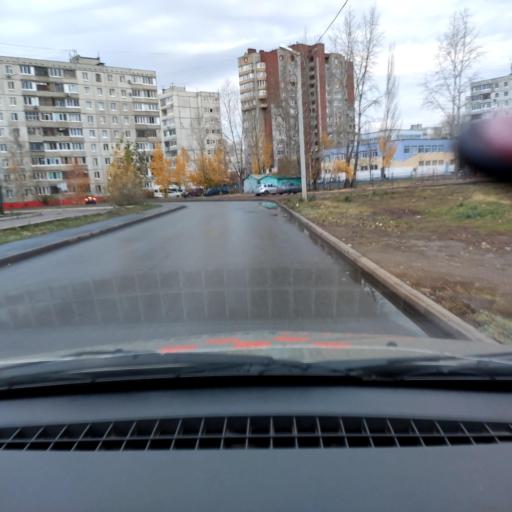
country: RU
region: Bashkortostan
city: Ufa
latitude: 54.7687
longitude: 56.0787
